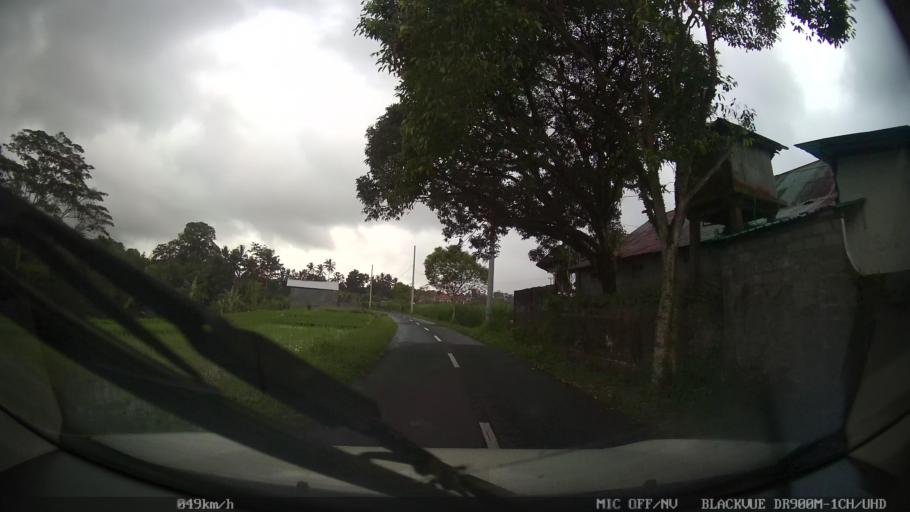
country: ID
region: Bali
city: Banjar Badung Tengah
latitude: -8.5131
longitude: 115.1982
